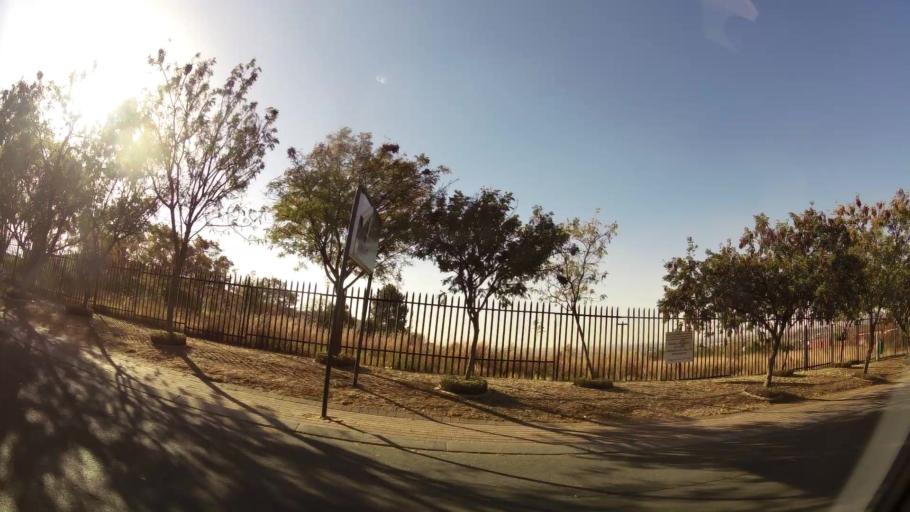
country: ZA
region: Gauteng
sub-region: City of Johannesburg Metropolitan Municipality
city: Diepsloot
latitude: -25.9881
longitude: 27.9862
